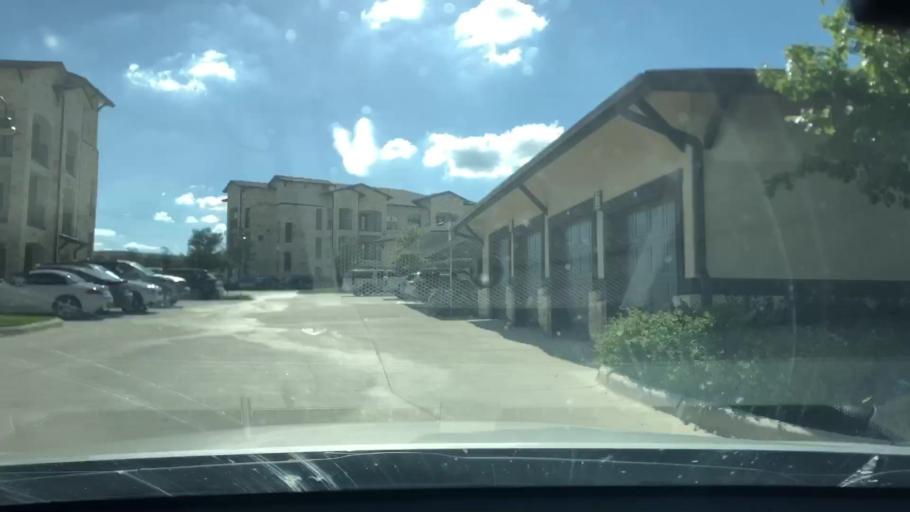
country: US
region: Texas
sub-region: Bexar County
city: Hollywood Park
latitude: 29.6194
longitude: -98.4748
